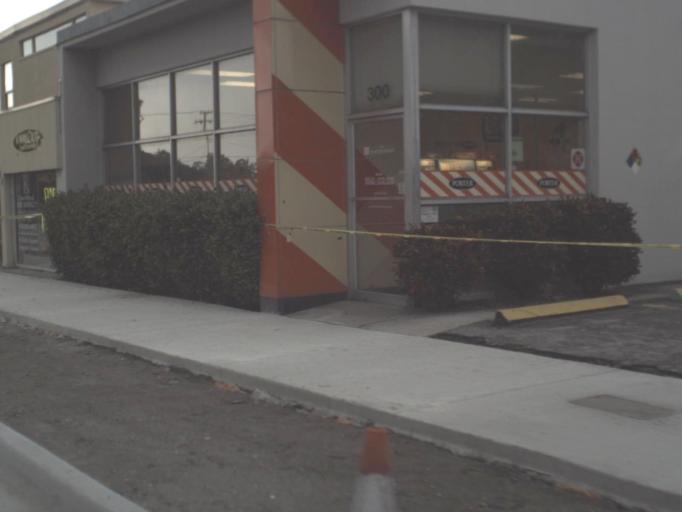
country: US
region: Florida
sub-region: Sarasota County
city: Sarasota
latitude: 27.3338
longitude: -82.5311
